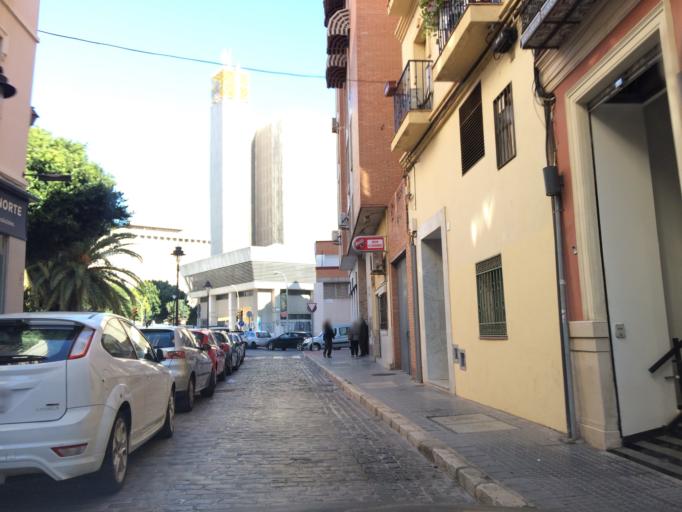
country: ES
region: Andalusia
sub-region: Provincia de Malaga
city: Malaga
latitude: 36.7153
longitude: -4.4278
